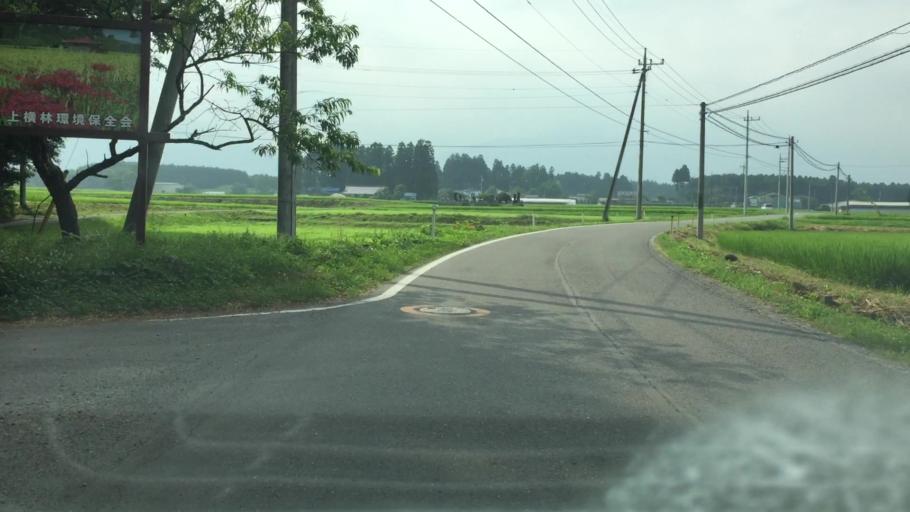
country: JP
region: Tochigi
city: Kuroiso
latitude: 36.9585
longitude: 139.9546
